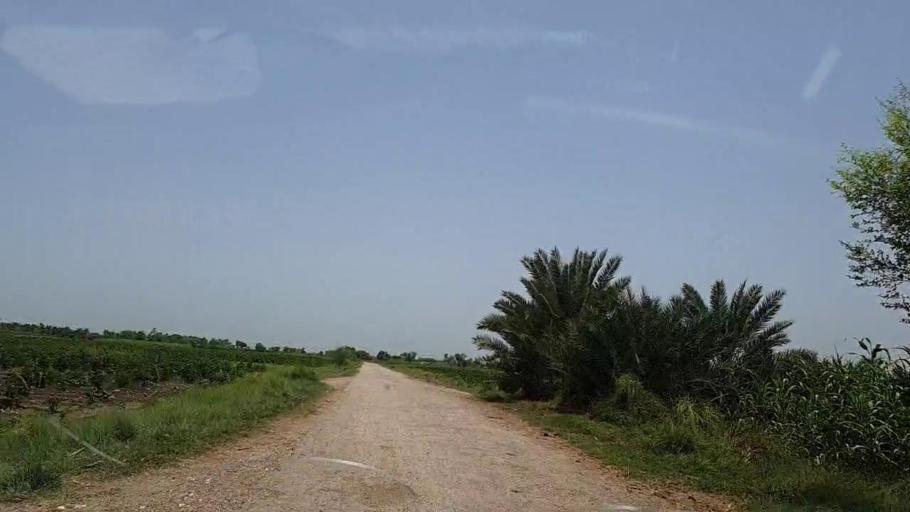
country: PK
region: Sindh
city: Tharu Shah
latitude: 26.9226
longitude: 68.0412
